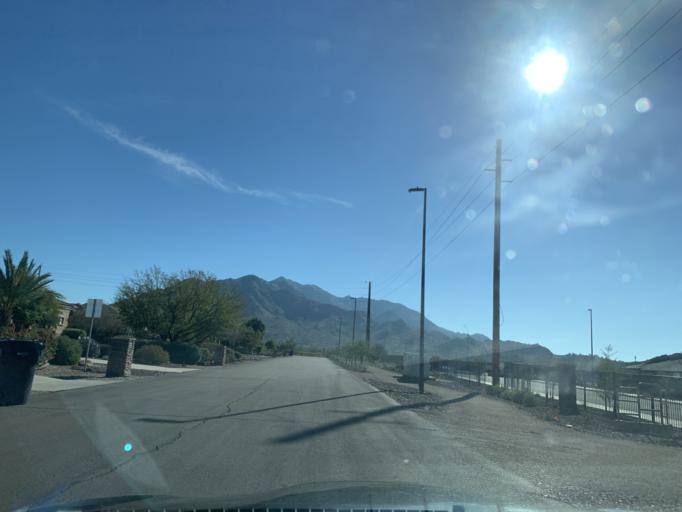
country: US
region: Arizona
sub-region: Maricopa County
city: Queen Creek
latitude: 33.2060
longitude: -111.7119
